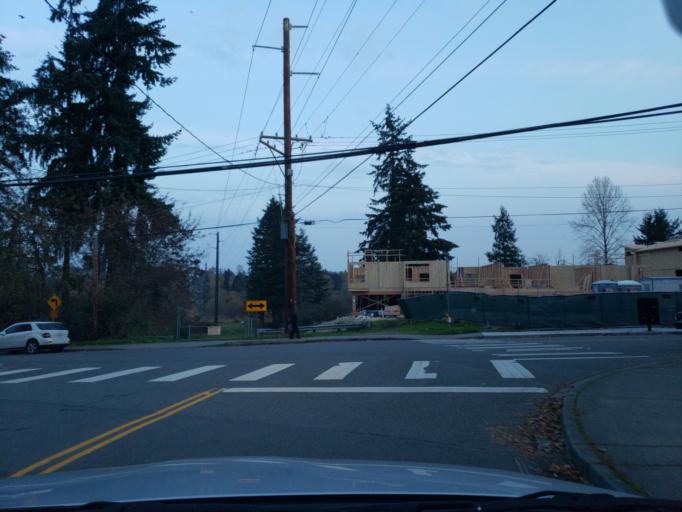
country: US
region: Washington
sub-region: King County
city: Kenmore
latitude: 47.7625
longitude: -122.2435
